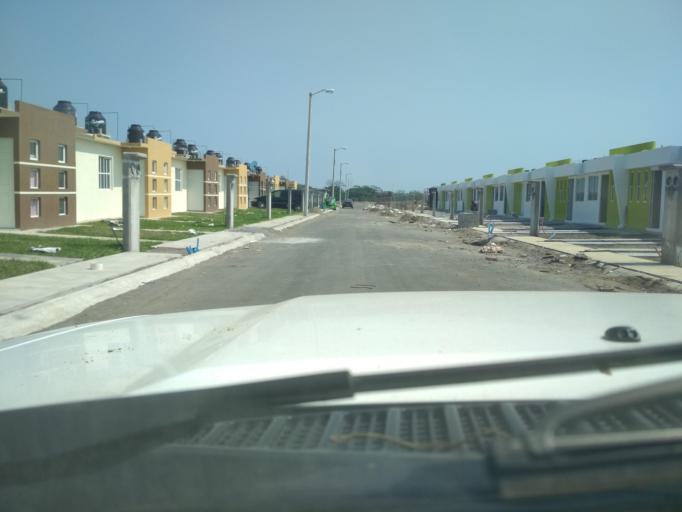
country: MX
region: Veracruz
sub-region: Veracruz
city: Lomas de Rio Medio Cuatro
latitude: 19.1919
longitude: -96.2074
